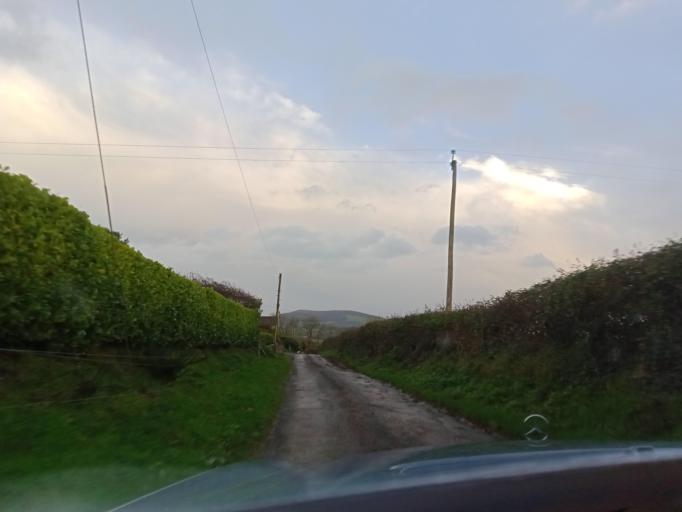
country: IE
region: Leinster
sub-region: Loch Garman
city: New Ross
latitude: 52.3470
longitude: -7.0082
